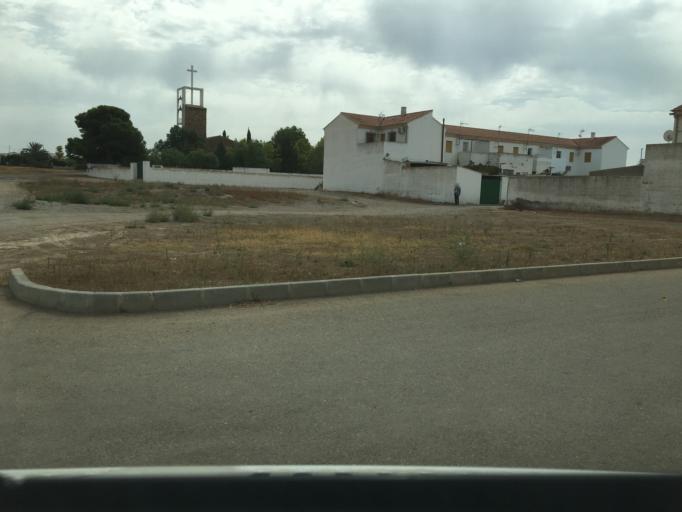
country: ES
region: Andalusia
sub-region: Provincia de Almeria
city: Huercal-Overa
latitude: 37.4225
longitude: -1.8799
